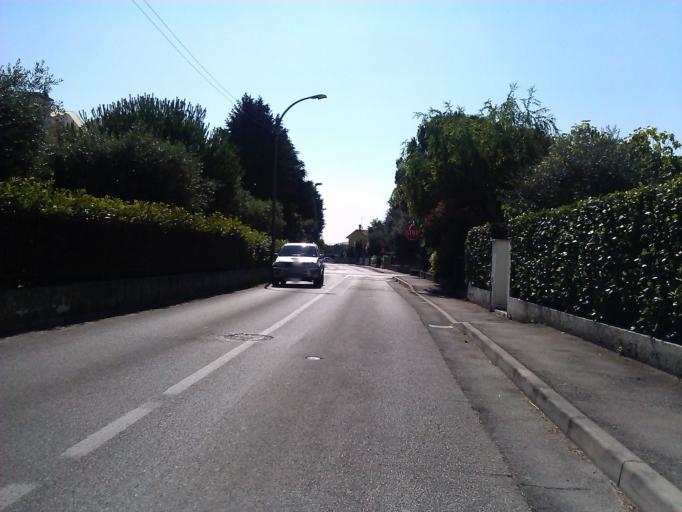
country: IT
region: Veneto
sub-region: Provincia di Vicenza
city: Bassano del Grappa
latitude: 45.7747
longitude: 11.7441
